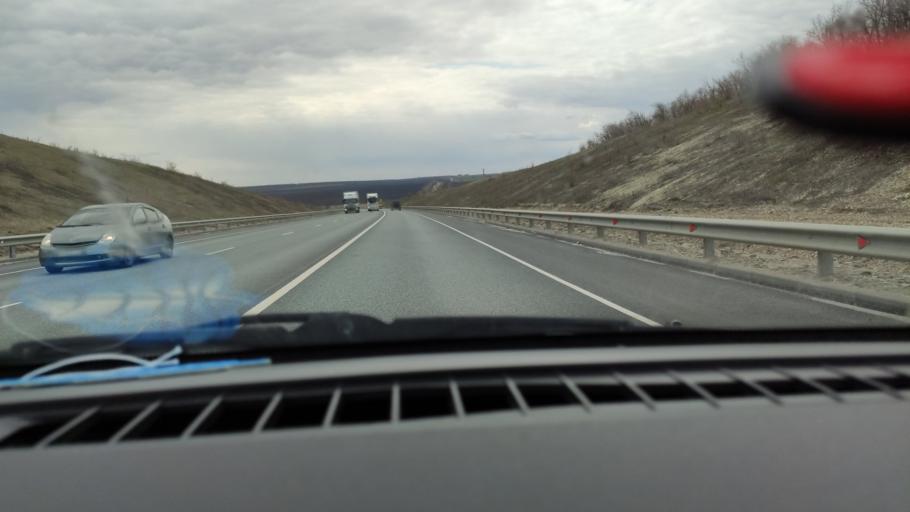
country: RU
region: Saratov
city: Yelshanka
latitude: 51.8810
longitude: 46.5101
